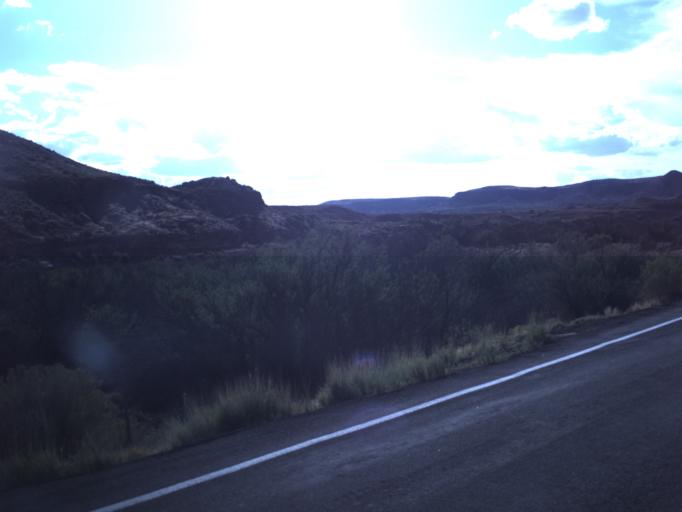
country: US
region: Utah
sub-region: San Juan County
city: Blanding
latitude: 37.3065
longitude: -109.2896
